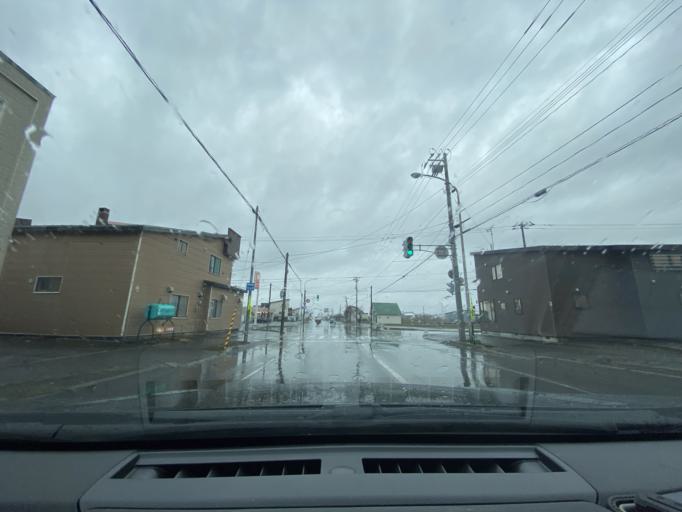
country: JP
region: Hokkaido
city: Fukagawa
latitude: 43.8090
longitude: 142.0235
